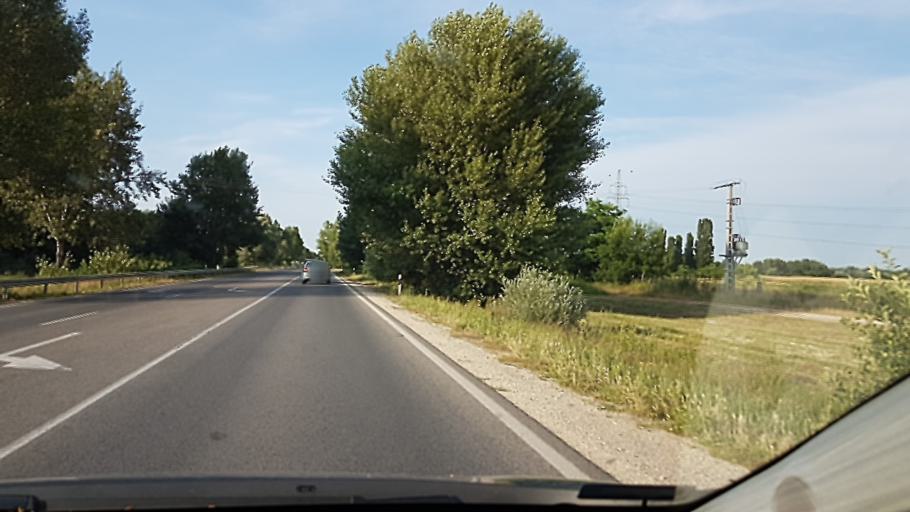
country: HU
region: Pest
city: Dunaharaszti
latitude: 47.3301
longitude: 19.1028
